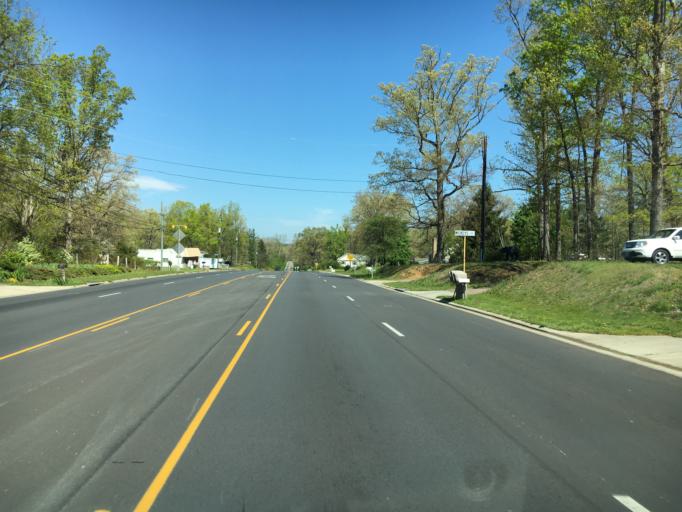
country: US
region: Virginia
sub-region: Augusta County
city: Crimora
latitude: 38.1555
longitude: -78.8437
